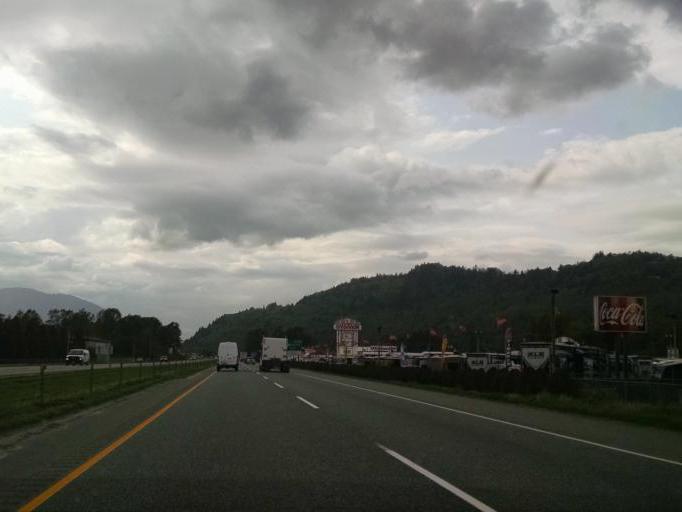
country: CA
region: British Columbia
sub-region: Fraser Valley Regional District
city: Chilliwack
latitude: 49.1441
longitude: -121.9904
